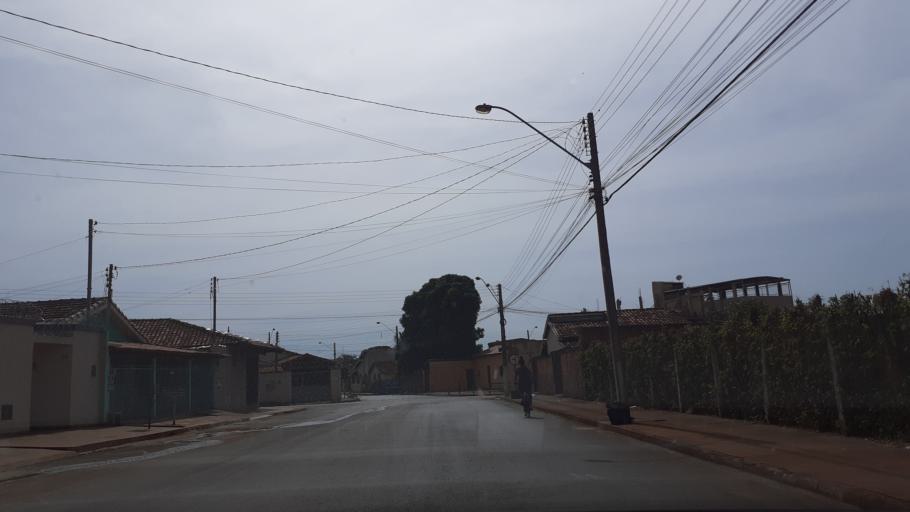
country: BR
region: Goias
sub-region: Itumbiara
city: Itumbiara
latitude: -18.4141
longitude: -49.2310
